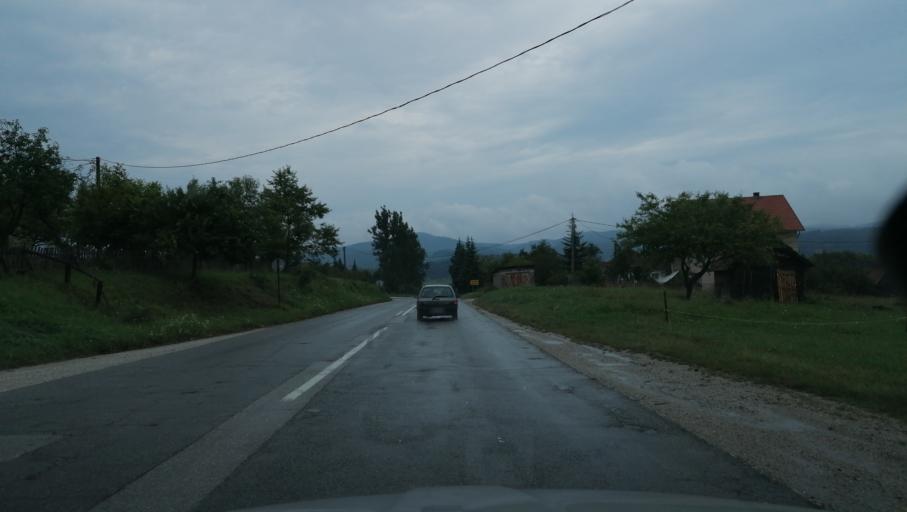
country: RS
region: Central Serbia
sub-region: Zlatiborski Okrug
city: Bajina Basta
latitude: 43.8446
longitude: 19.5946
